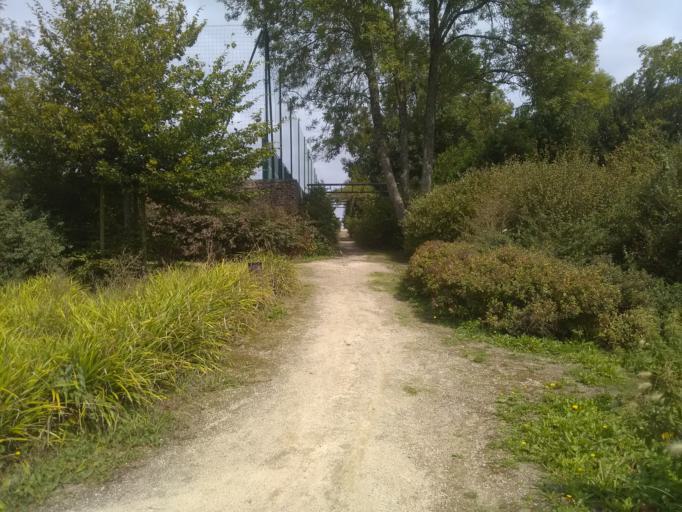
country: FR
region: Brittany
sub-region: Departement d'Ille-et-Vilaine
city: Dinge
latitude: 48.3553
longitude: -1.7180
